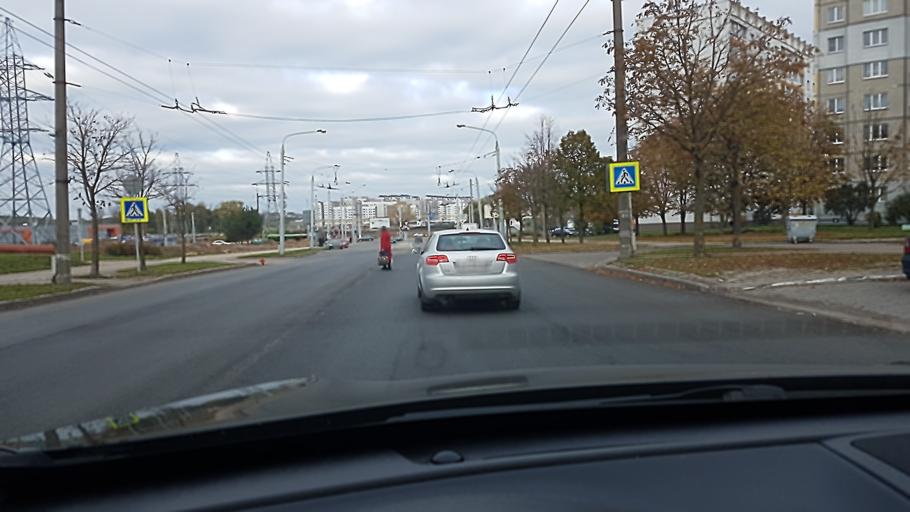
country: BY
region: Minsk
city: Novoye Medvezhino
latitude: 53.8727
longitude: 27.4644
